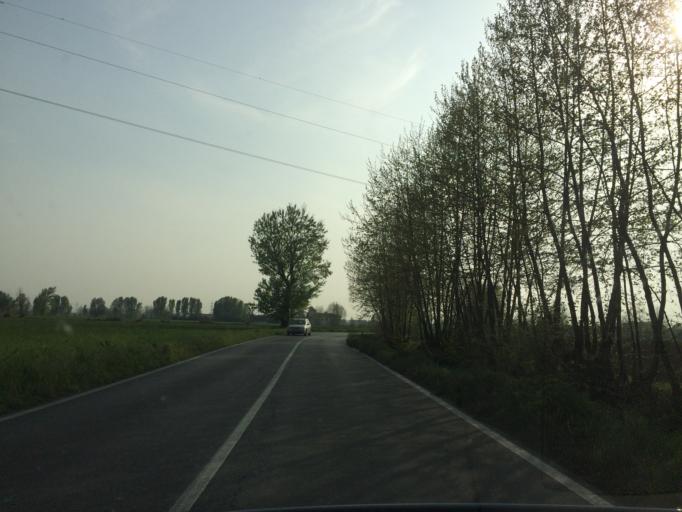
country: IT
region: Lombardy
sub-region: Provincia di Brescia
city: Folzano
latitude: 45.5120
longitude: 10.2017
